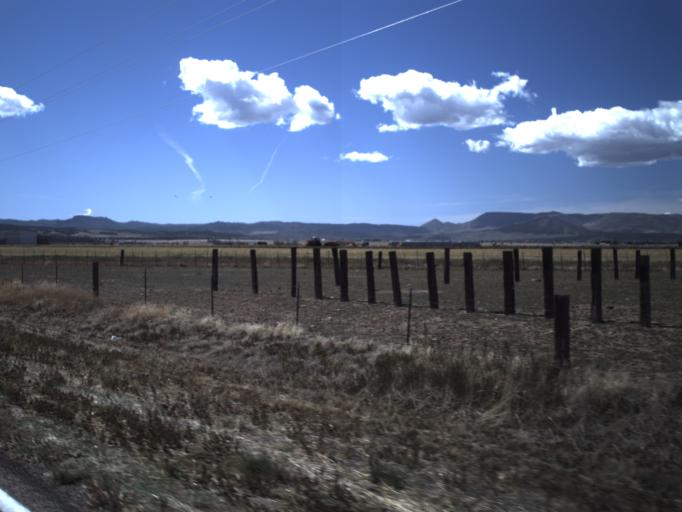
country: US
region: Utah
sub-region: Washington County
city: Enterprise
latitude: 37.6110
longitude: -113.6612
